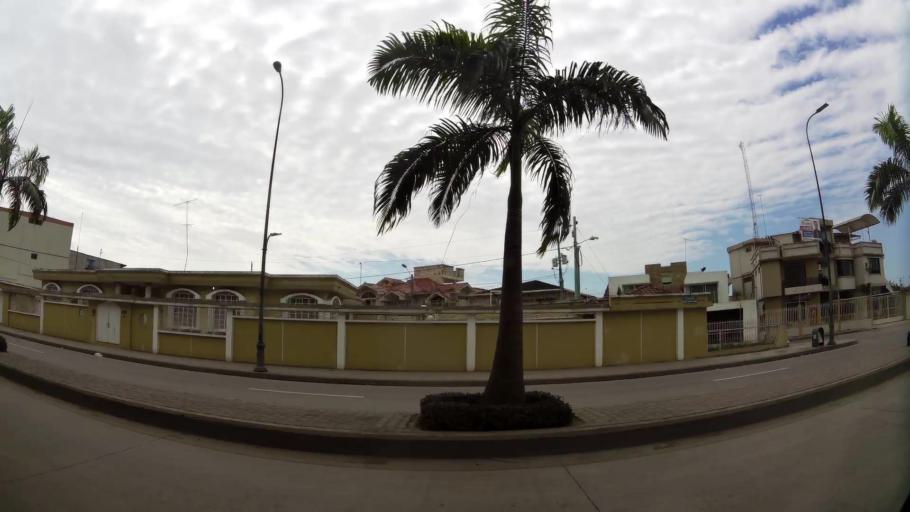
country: EC
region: El Oro
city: Machala
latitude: -3.2594
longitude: -79.9412
